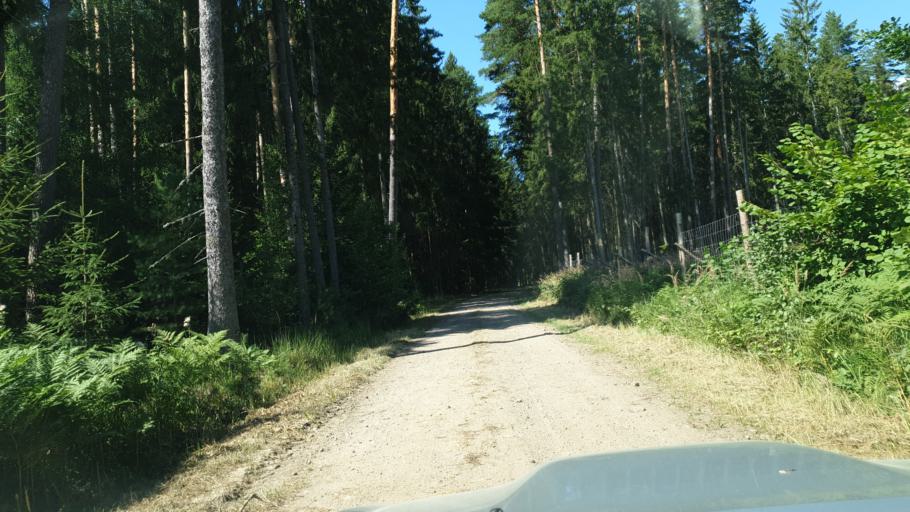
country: LT
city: Sirvintos
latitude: 54.9083
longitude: 24.9400
